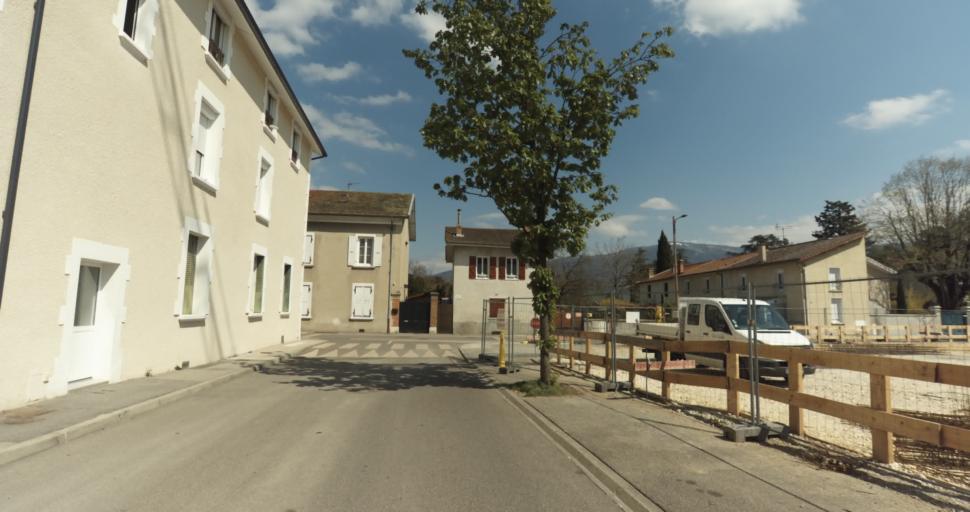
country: FR
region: Rhone-Alpes
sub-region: Departement de l'Isere
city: Saint-Marcellin
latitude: 45.1501
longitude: 5.3244
